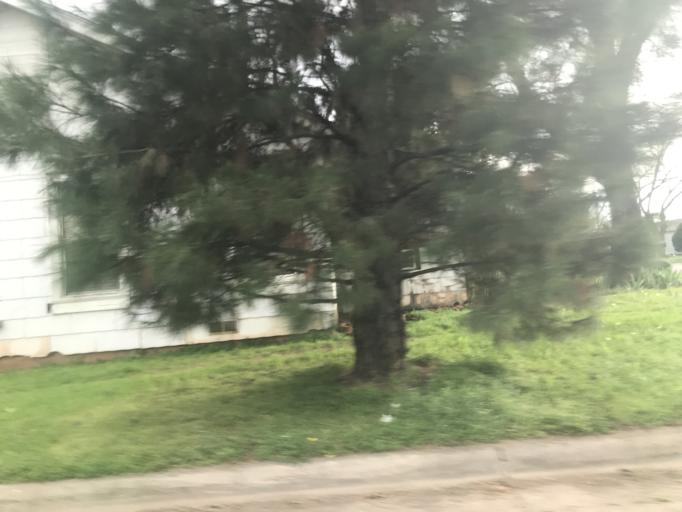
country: US
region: Texas
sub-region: Taylor County
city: Abilene
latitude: 32.4428
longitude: -99.7614
